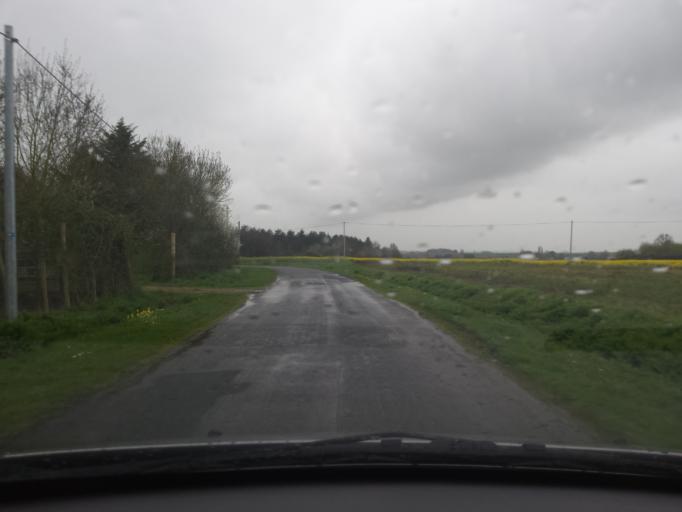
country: FR
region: Pays de la Loire
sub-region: Departement de la Vendee
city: Sainte-Hermine
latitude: 46.5817
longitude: -1.0813
